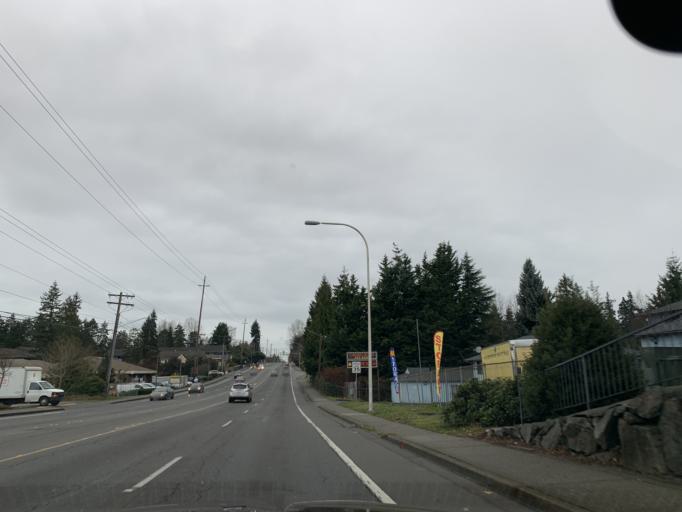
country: US
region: Washington
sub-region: Snohomish County
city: Everett
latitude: 47.9221
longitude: -122.2308
